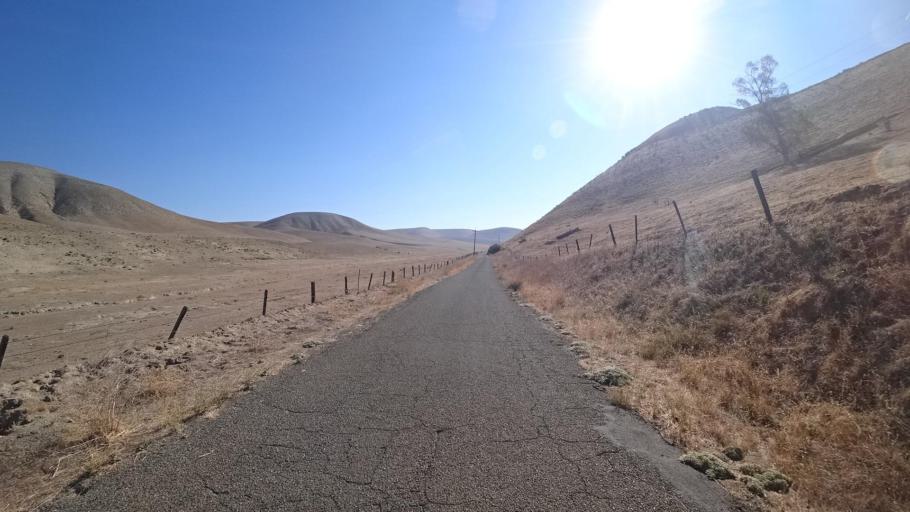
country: US
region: California
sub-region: Monterey County
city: King City
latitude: 36.2000
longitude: -121.0134
